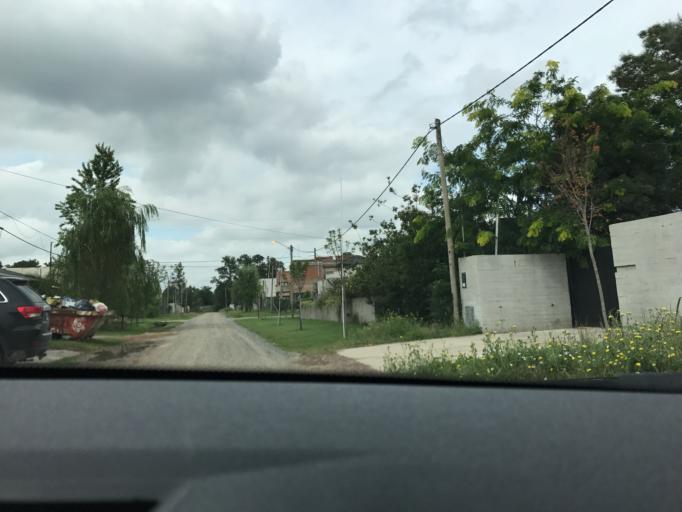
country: AR
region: Buenos Aires
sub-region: Partido de La Plata
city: La Plata
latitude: -34.8586
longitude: -58.0518
